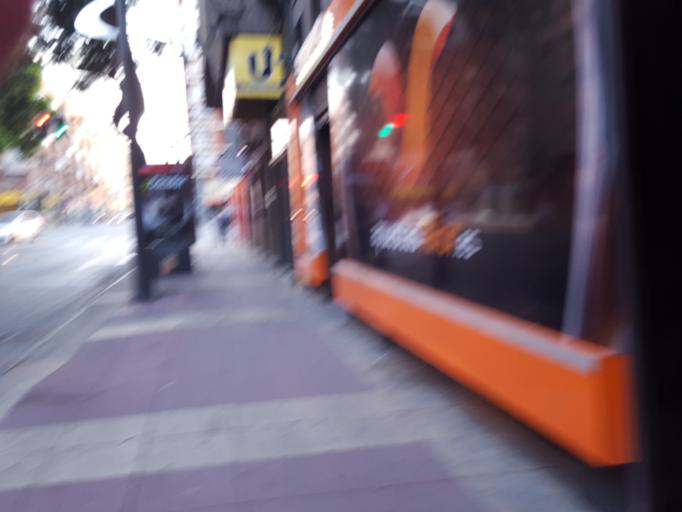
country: ES
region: Murcia
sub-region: Murcia
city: Murcia
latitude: 37.9767
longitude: -1.1327
